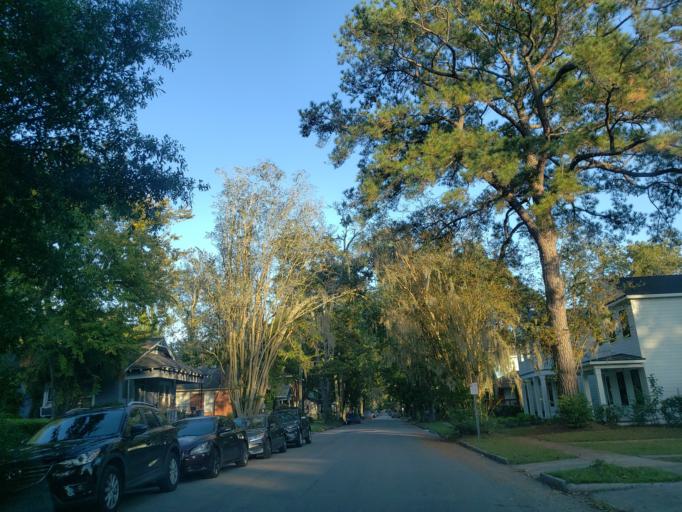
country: US
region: Georgia
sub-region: Chatham County
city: Savannah
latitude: 32.0565
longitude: -81.0903
